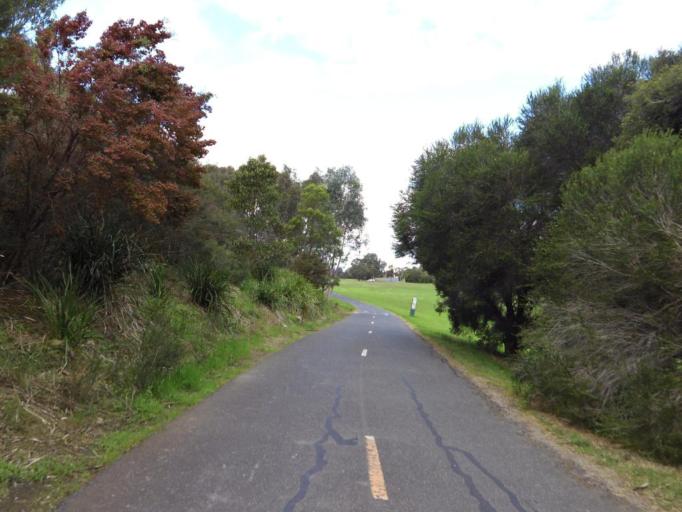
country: AU
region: Victoria
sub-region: Manningham
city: Bulleen
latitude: -37.7805
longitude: 145.0844
